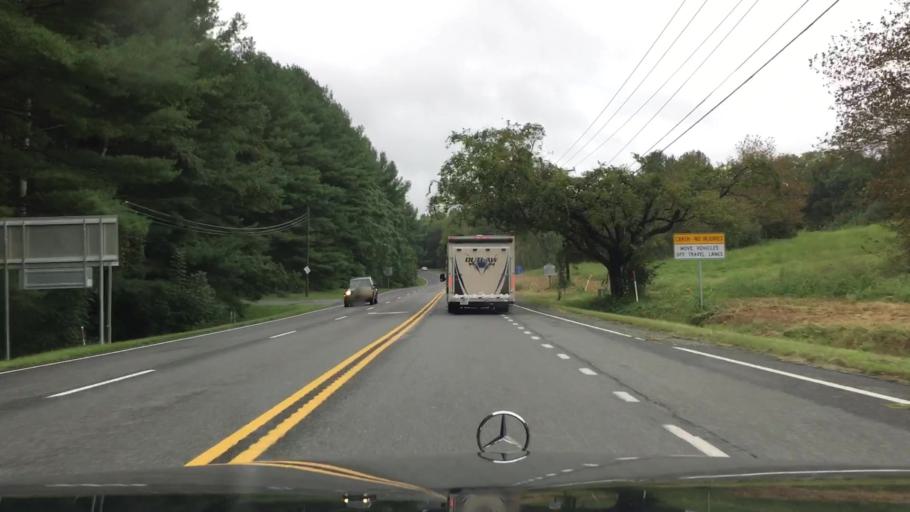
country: US
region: Virginia
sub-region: City of Charlottesville
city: Charlottesville
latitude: 38.0151
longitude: -78.3984
